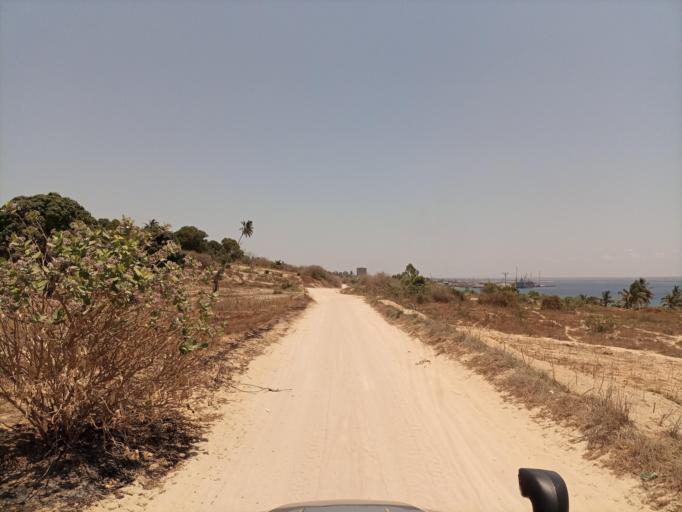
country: MZ
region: Nampula
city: Nacala
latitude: -14.5223
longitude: 40.6791
